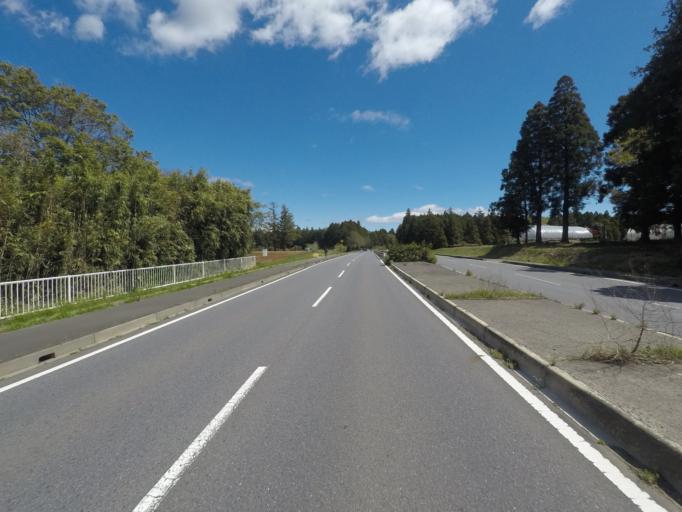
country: JP
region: Ibaraki
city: Ami
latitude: 36.0945
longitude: 140.2460
